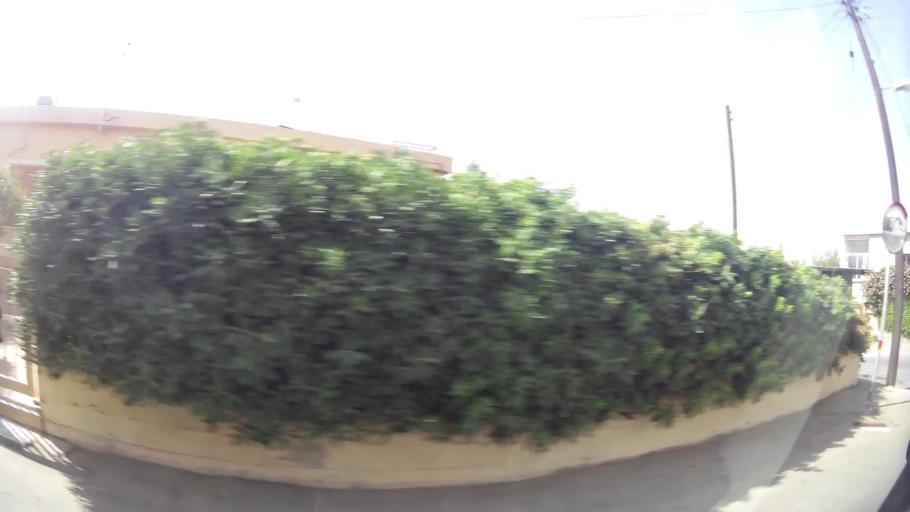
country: CY
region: Lefkosia
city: Tseri
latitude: 35.0728
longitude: 33.3214
